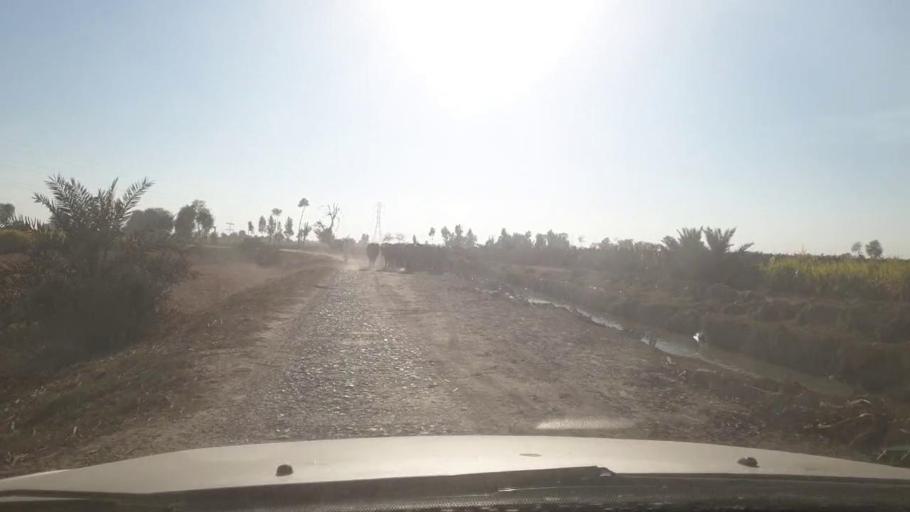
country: PK
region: Sindh
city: Adilpur
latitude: 27.9550
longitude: 69.2200
